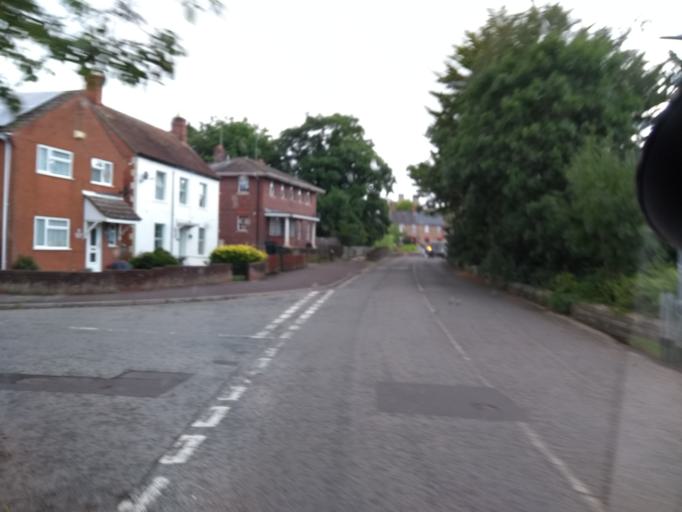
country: GB
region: England
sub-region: Somerset
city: Wincanton
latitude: 51.0560
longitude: -2.4154
